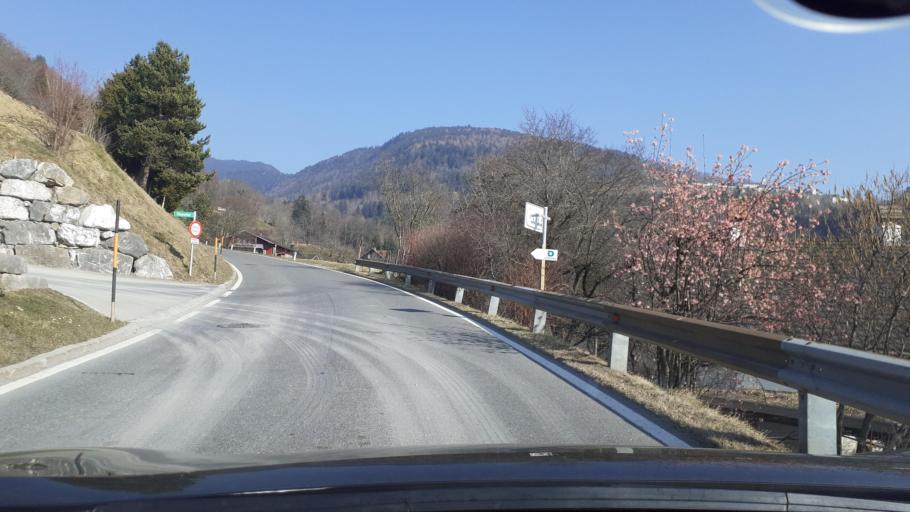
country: AT
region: Vorarlberg
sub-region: Politischer Bezirk Feldkirch
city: Viktorsberg
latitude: 47.3072
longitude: 9.6603
